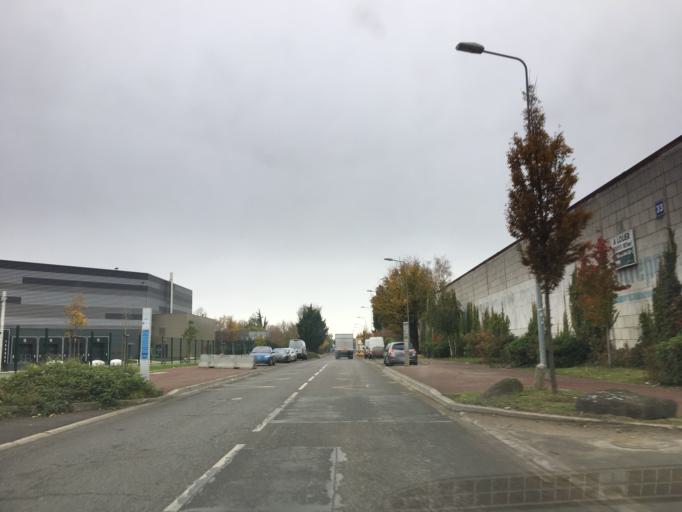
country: FR
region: Ile-de-France
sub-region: Departement du Val-de-Marne
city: Saint-Maur-des-Fosses
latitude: 48.7828
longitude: 2.5000
